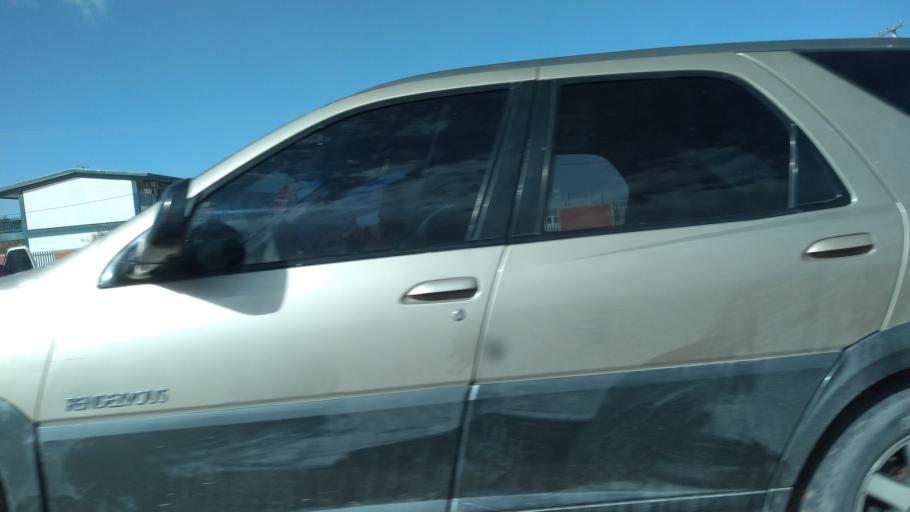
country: US
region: Texas
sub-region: El Paso County
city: Socorro Mission Number 1 Colonia
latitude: 31.5876
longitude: -106.3573
